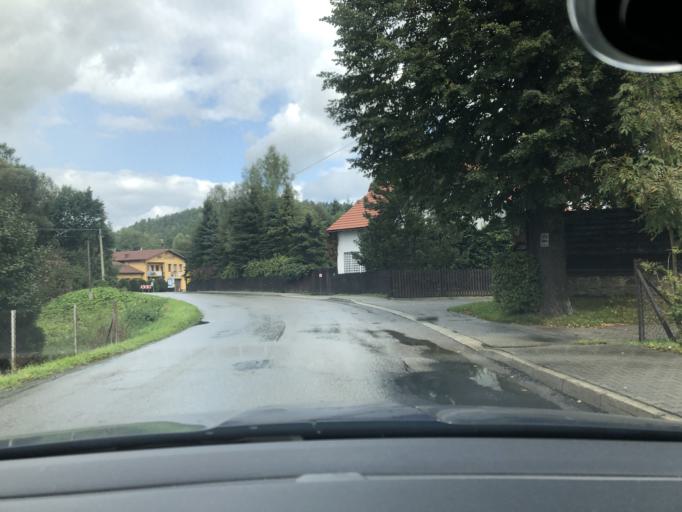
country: PL
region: Lesser Poland Voivodeship
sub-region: Powiat suski
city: Lachowice
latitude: 49.7134
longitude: 19.4720
